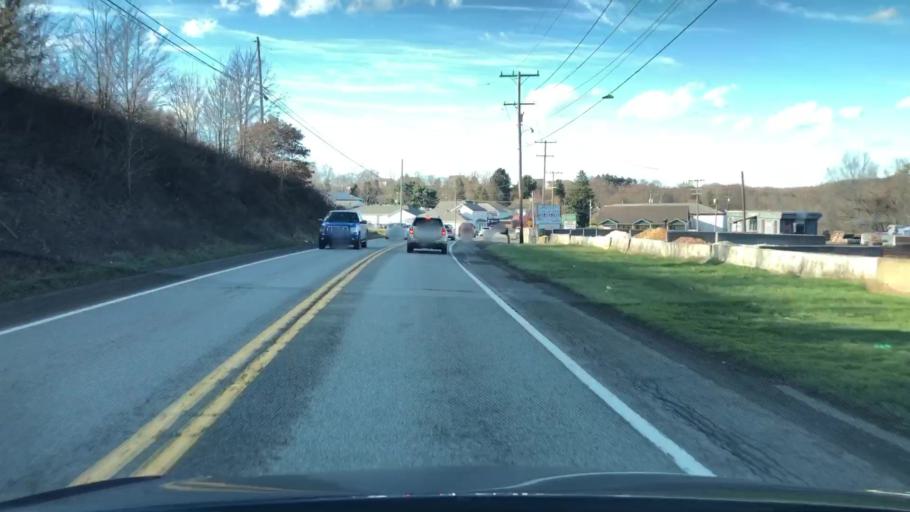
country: US
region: Pennsylvania
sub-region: Butler County
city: Saxonburg
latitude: 40.7160
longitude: -79.7522
